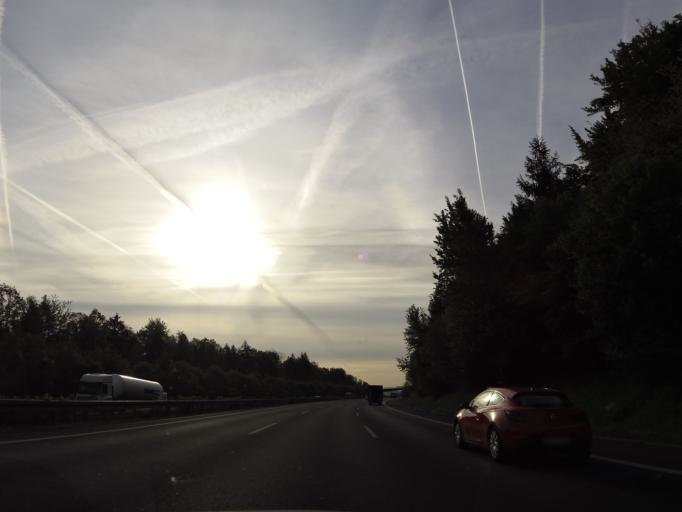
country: DE
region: Lower Saxony
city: Hannoversch Munden
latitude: 51.3986
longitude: 9.6813
